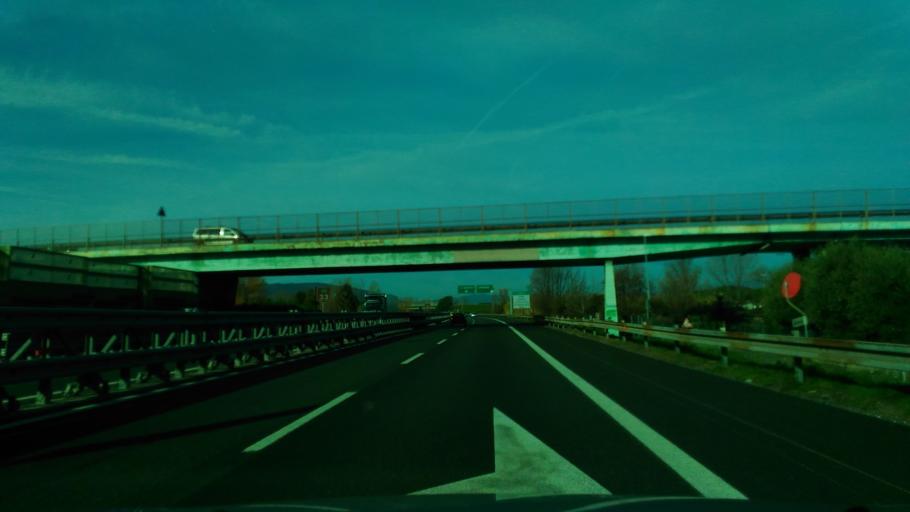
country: IT
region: Tuscany
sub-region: Provincia di Massa-Carrara
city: Marina di Carrara
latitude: 44.0507
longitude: 10.0382
